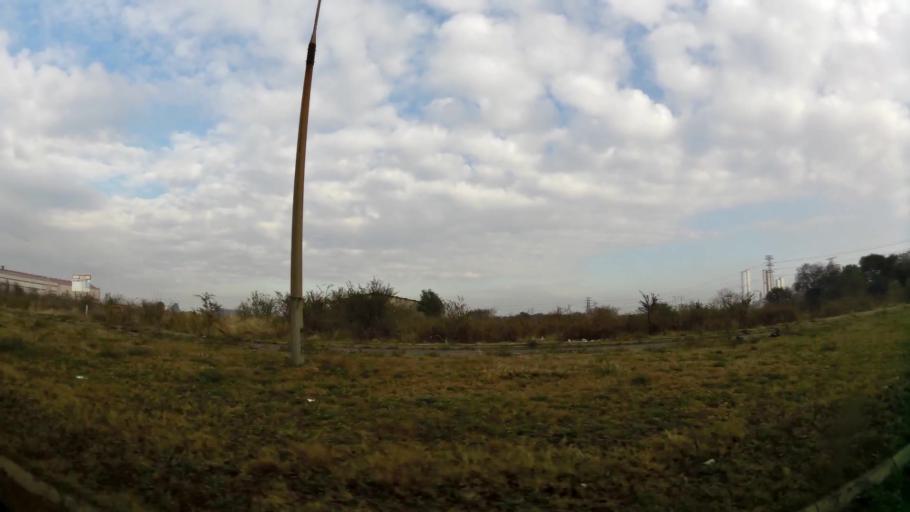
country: ZA
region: Gauteng
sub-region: Sedibeng District Municipality
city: Vanderbijlpark
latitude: -26.6751
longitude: 27.8109
